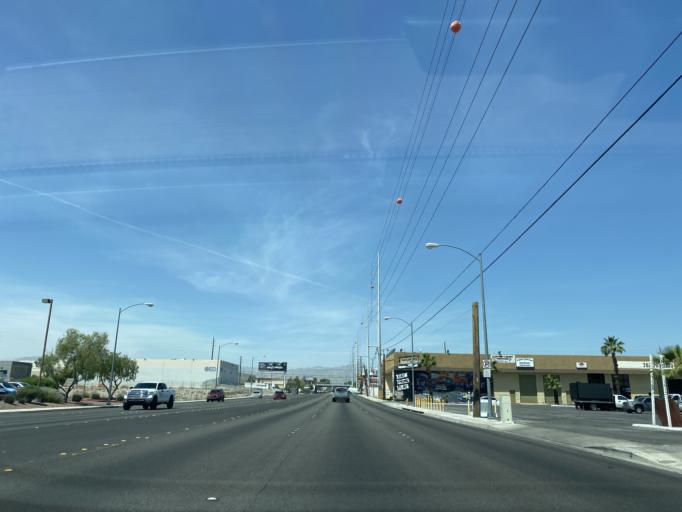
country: US
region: Nevada
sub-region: Clark County
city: Paradise
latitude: 36.0864
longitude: -115.1919
